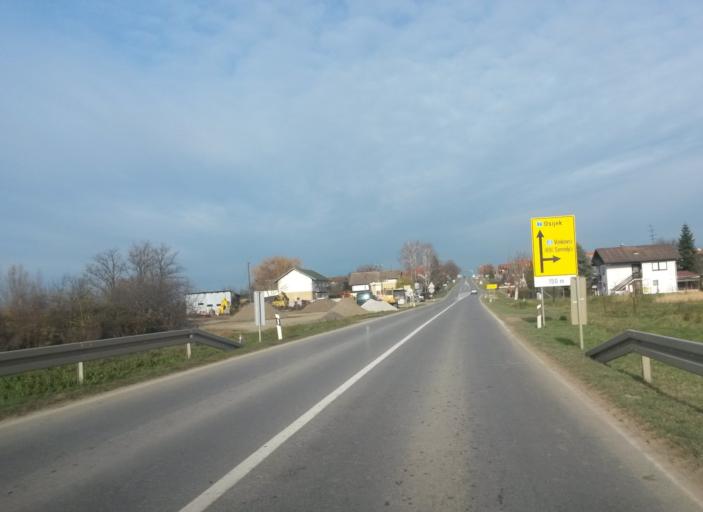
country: HR
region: Osjecko-Baranjska
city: Viskovci
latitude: 45.3440
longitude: 18.4212
